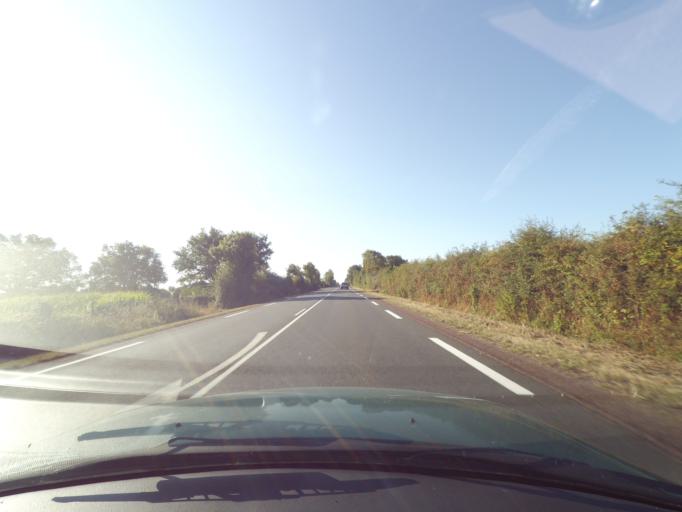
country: FR
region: Poitou-Charentes
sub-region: Departement des Deux-Sevres
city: Viennay
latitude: 46.6785
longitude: -0.2627
